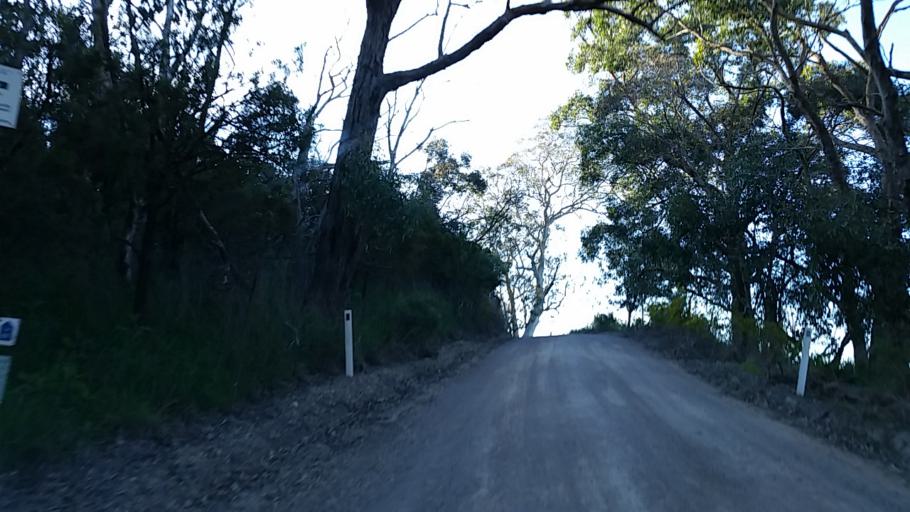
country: AU
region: South Australia
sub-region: Mount Barker
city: Meadows
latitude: -35.2295
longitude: 138.7388
